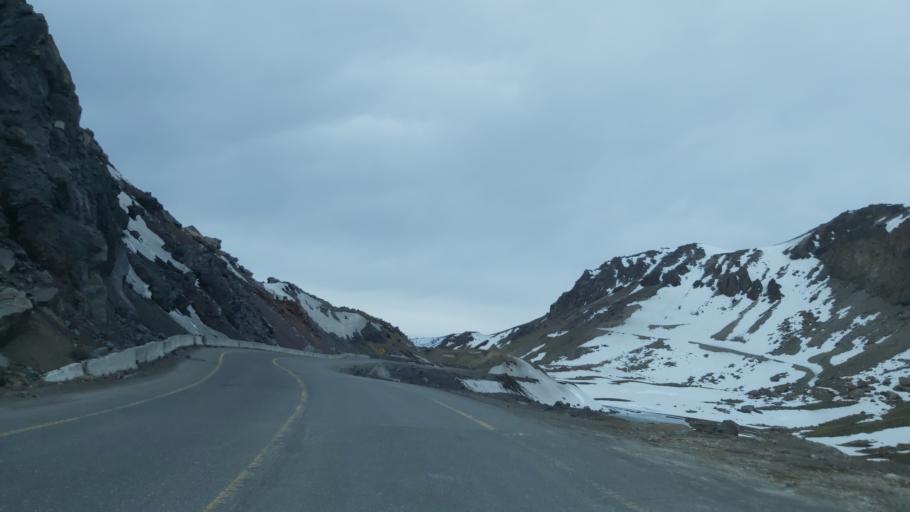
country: CL
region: Maule
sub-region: Provincia de Linares
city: Colbun
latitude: -36.0065
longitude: -70.5588
